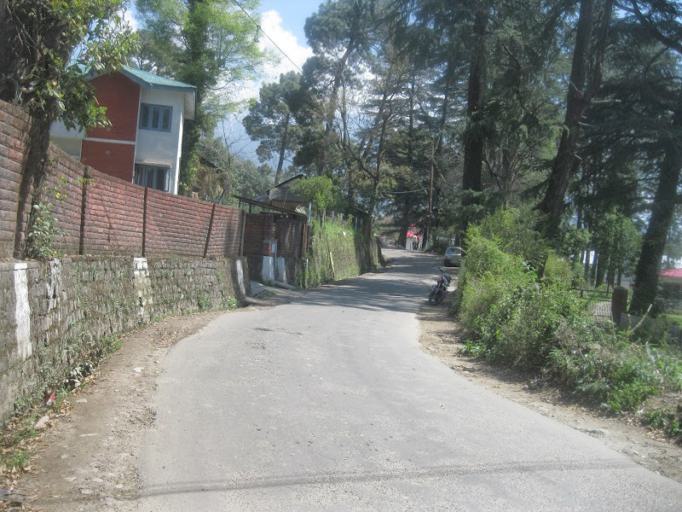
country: IN
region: Himachal Pradesh
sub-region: Kangra
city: Palampur
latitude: 32.1160
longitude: 76.5383
